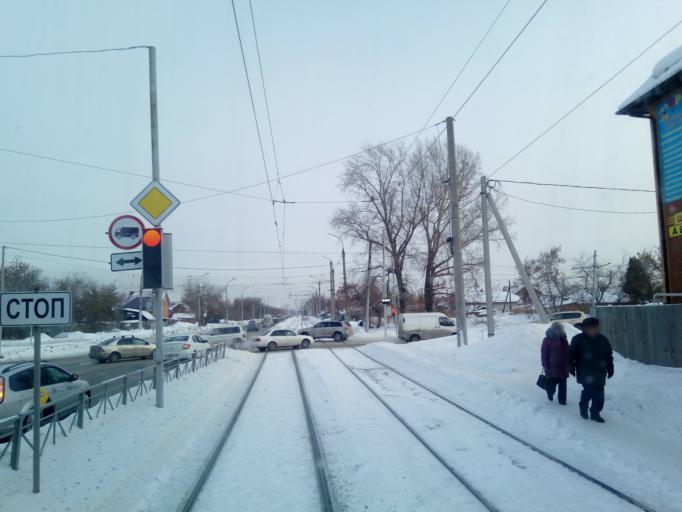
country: RU
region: Novosibirsk
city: Tolmachevo
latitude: 54.9802
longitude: 82.8349
